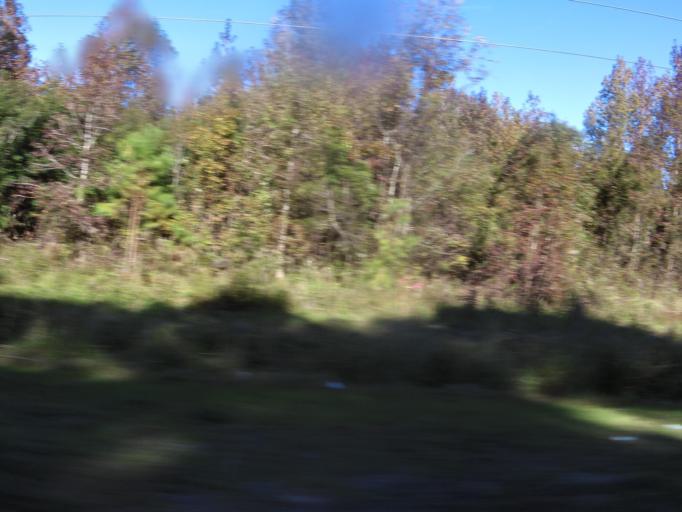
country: US
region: Georgia
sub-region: Liberty County
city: Midway
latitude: 31.7999
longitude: -81.4242
